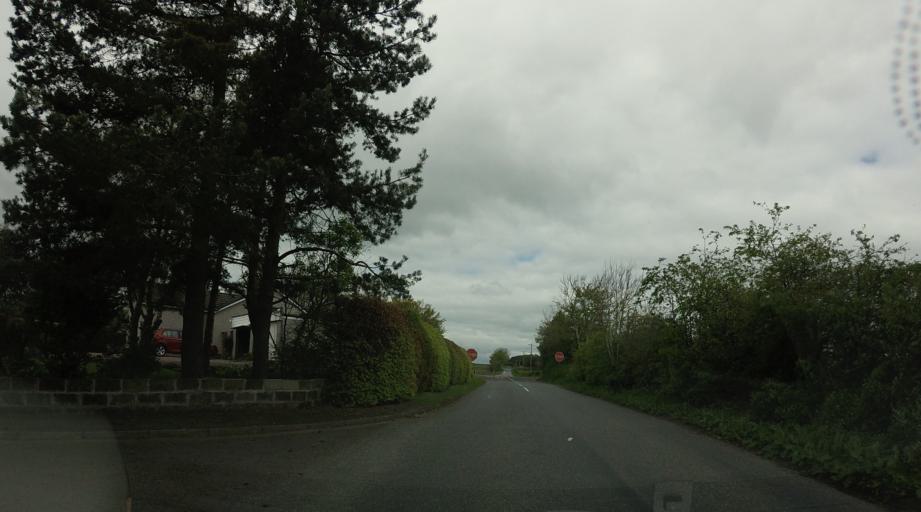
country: GB
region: Scotland
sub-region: Perth and Kinross
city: Milnathort
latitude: 56.2441
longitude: -3.3746
